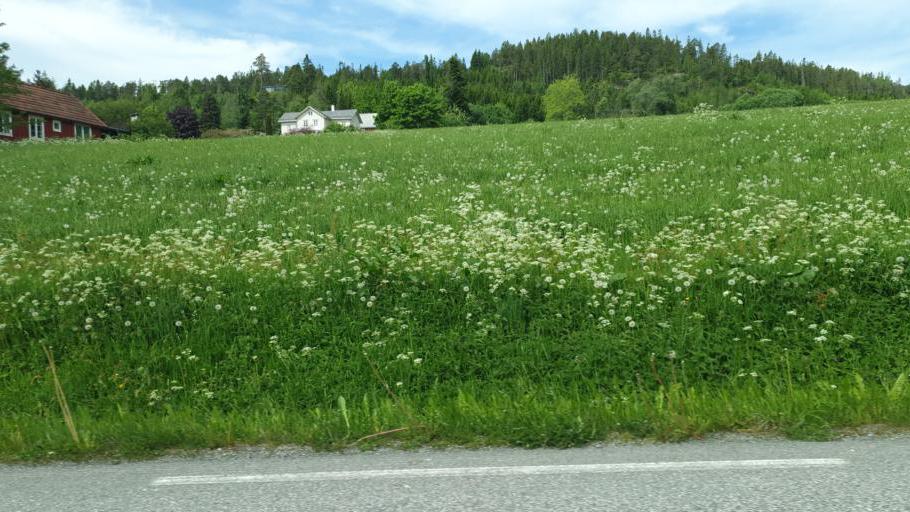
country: NO
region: Sor-Trondelag
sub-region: Trondheim
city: Trondheim
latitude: 63.5832
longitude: 10.4184
